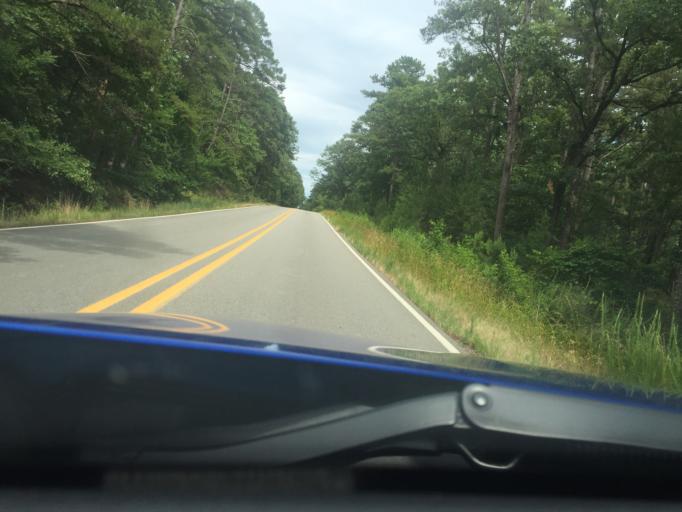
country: US
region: Arkansas
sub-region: Pulaski County
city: Maumelle
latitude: 34.8352
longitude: -92.4653
